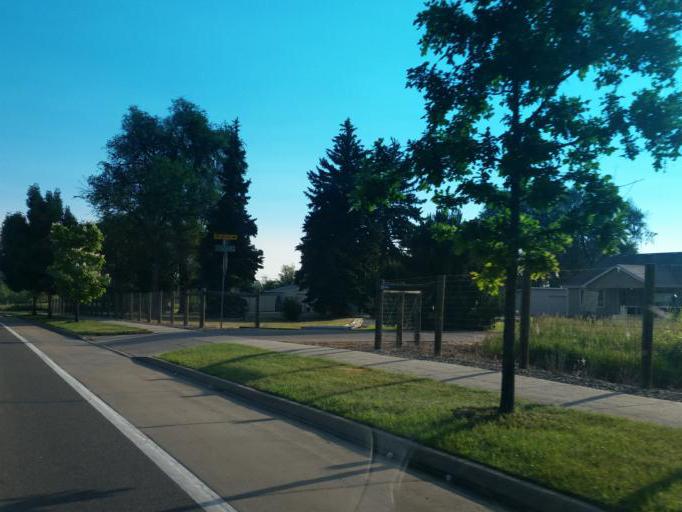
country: US
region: Colorado
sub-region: Larimer County
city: Fort Collins
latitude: 40.5487
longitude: -105.1150
